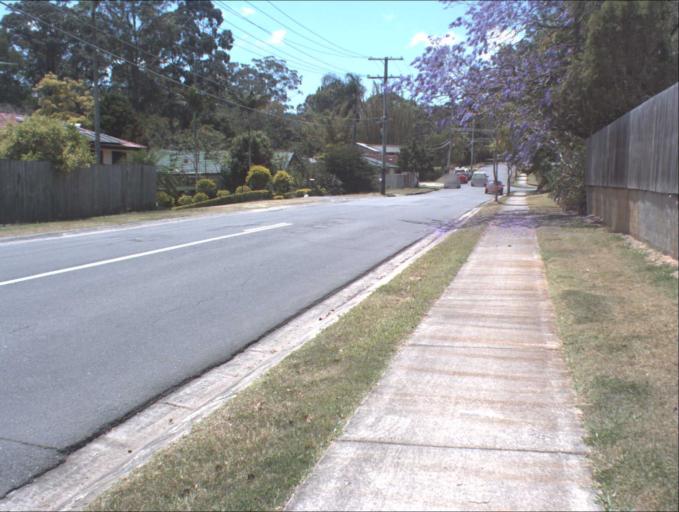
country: AU
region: Queensland
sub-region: Logan
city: Slacks Creek
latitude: -27.6417
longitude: 153.1623
